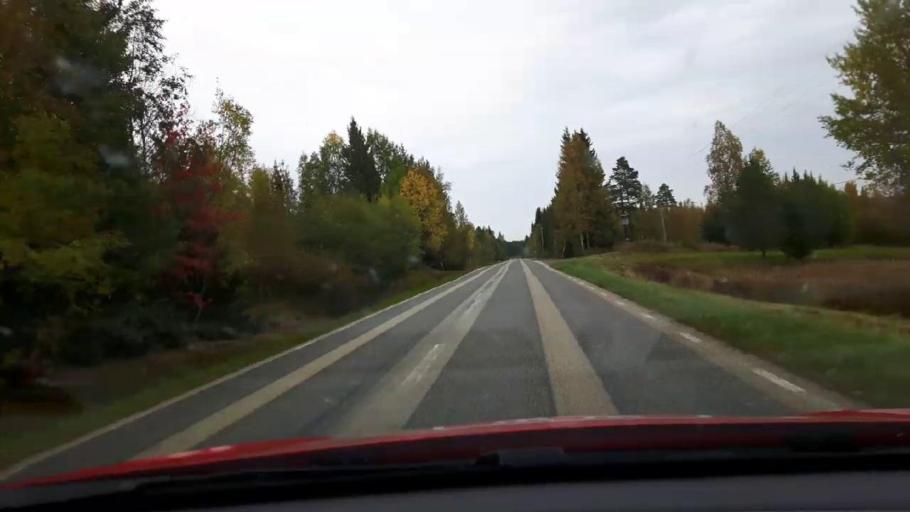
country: SE
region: Jaemtland
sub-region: Bergs Kommun
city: Hoverberg
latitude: 62.8684
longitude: 14.3727
